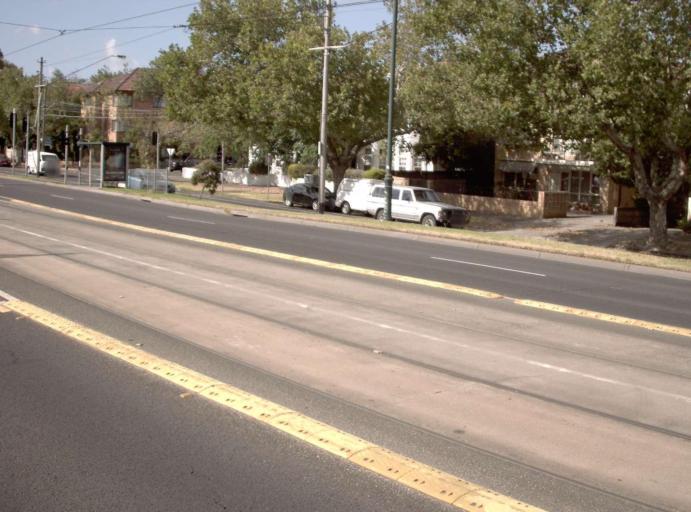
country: AU
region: Victoria
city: Ripponlea
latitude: -37.8784
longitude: 144.9937
